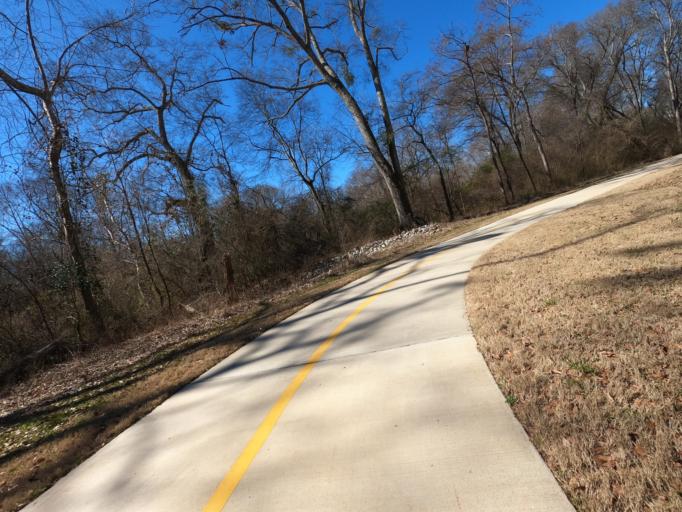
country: US
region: Georgia
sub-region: Clarke County
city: Athens
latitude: 33.9410
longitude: -83.3650
